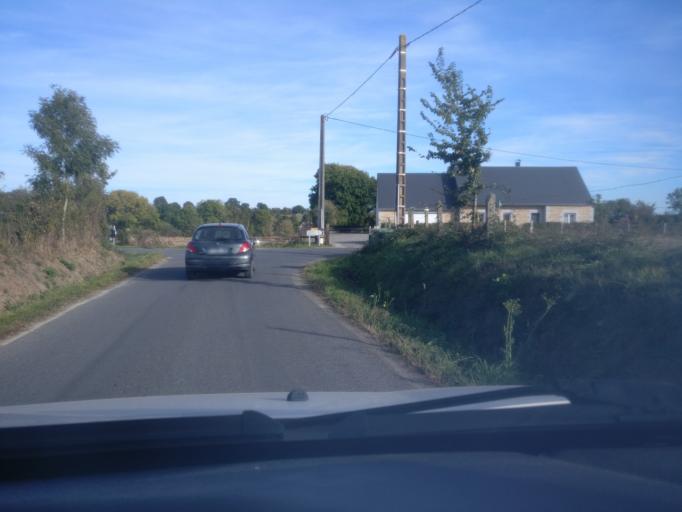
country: FR
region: Lower Normandy
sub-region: Departement de la Manche
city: Sartilly
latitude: 48.7112
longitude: -1.4866
